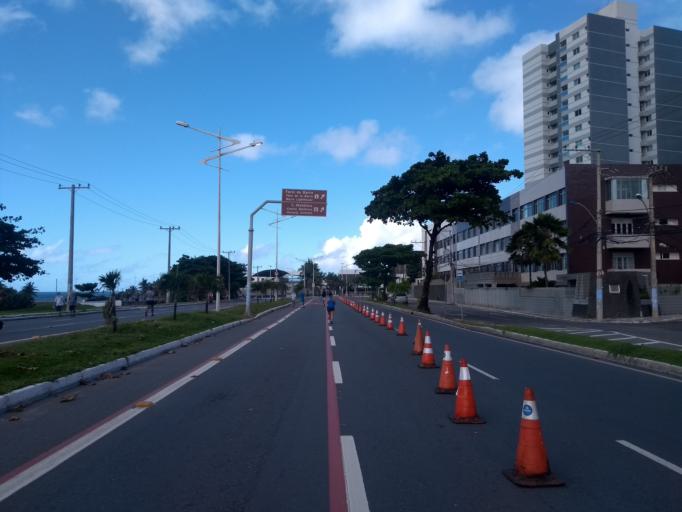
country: BR
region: Bahia
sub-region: Salvador
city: Salvador
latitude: -12.9976
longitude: -38.4503
